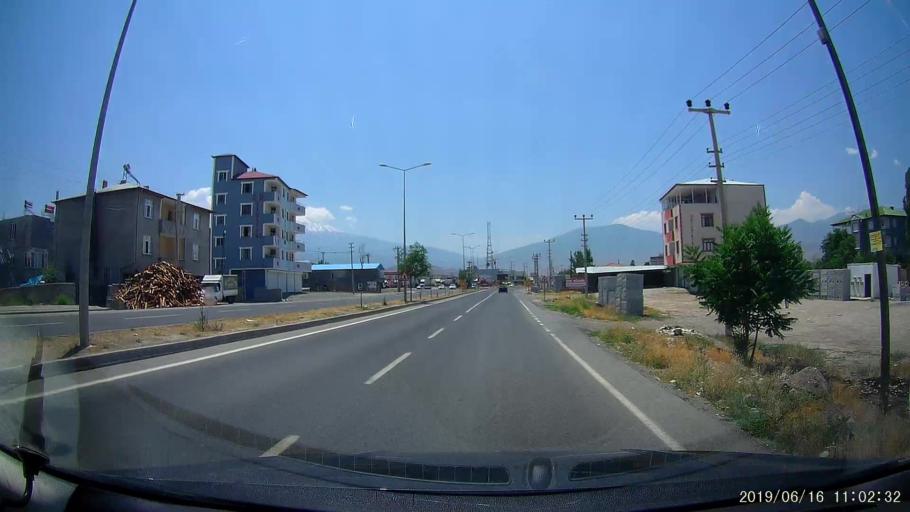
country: TR
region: Igdir
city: Igdir
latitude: 39.9114
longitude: 44.0584
